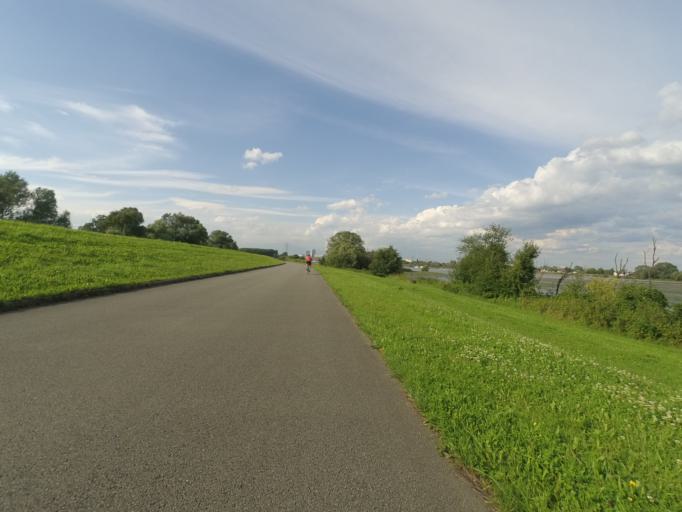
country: DE
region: Hamburg
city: Rothenburgsort
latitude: 53.5118
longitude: 10.0627
